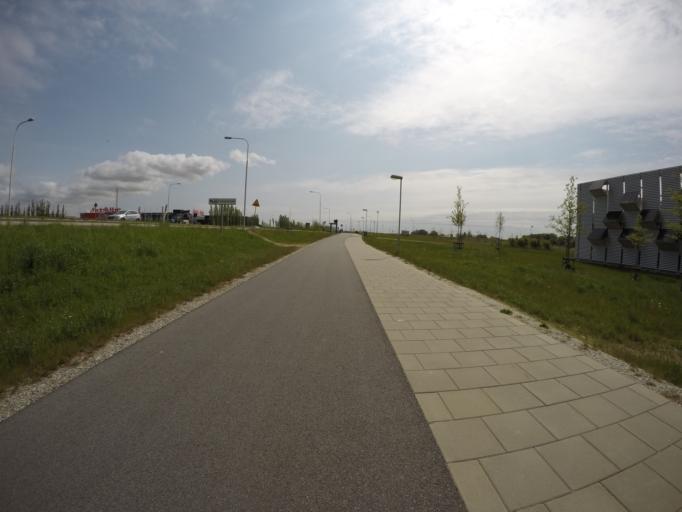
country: SE
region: Skane
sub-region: Malmo
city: Bunkeflostrand
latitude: 55.5525
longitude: 12.9828
